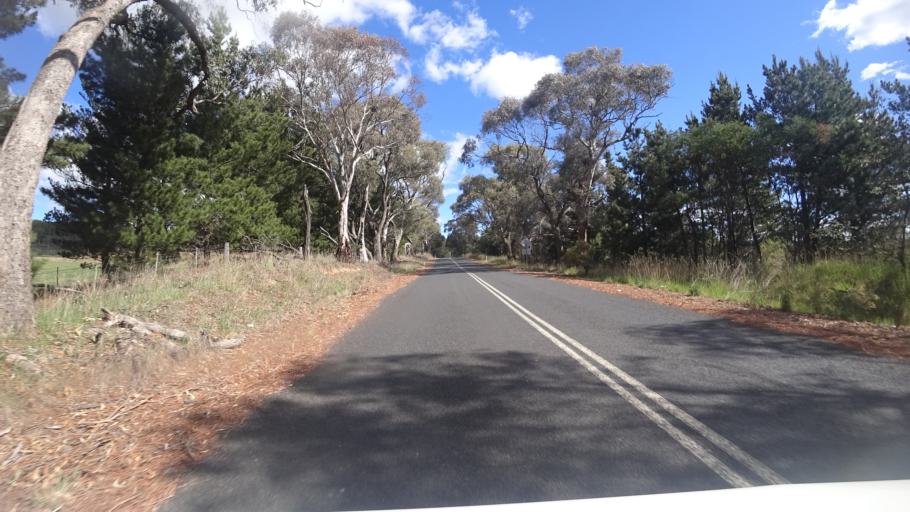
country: AU
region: New South Wales
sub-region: Oberon
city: Oberon
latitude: -33.6809
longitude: 149.7866
